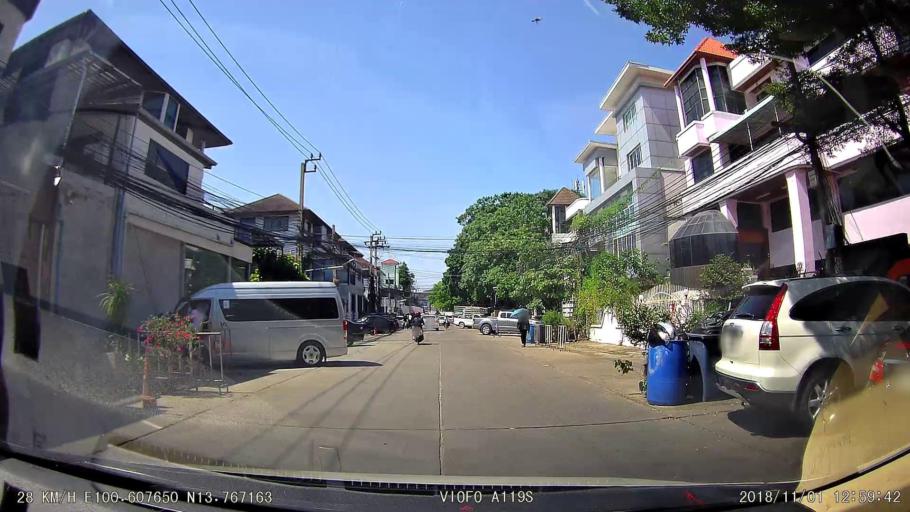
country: TH
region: Bangkok
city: Wang Thonglang
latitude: 13.7673
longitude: 100.6075
